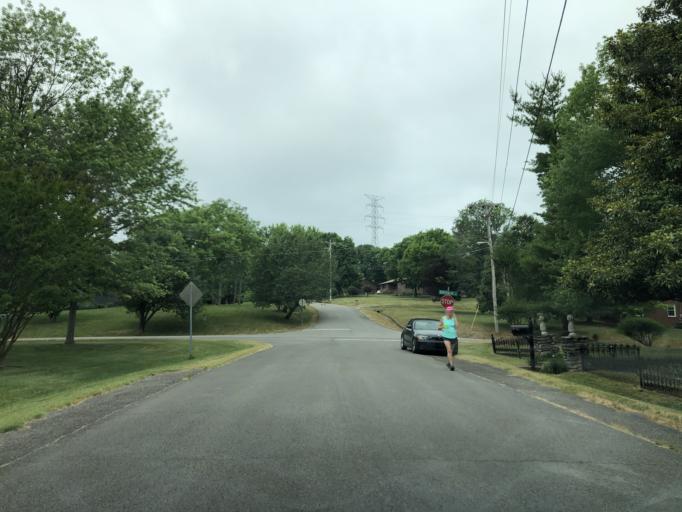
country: US
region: Tennessee
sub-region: Davidson County
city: Goodlettsville
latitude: 36.2858
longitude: -86.7344
